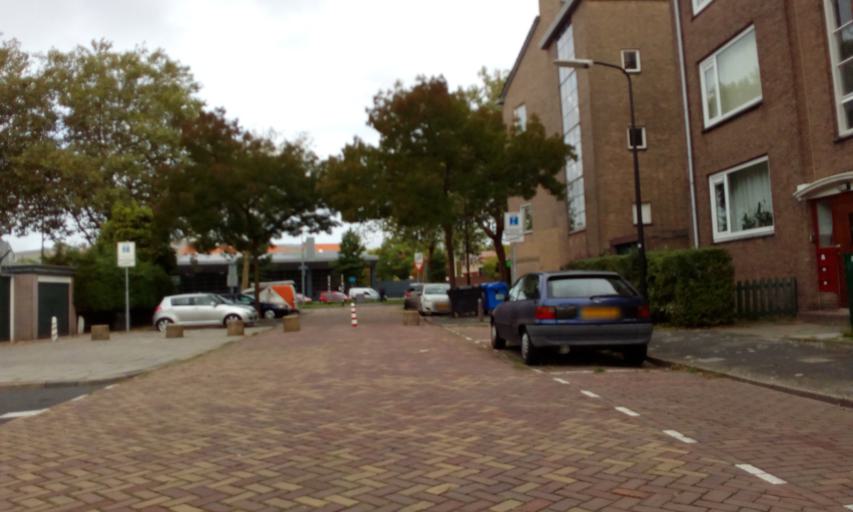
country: NL
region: South Holland
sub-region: Gemeente Rijswijk
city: Rijswijk
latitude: 52.0463
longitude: 4.3353
